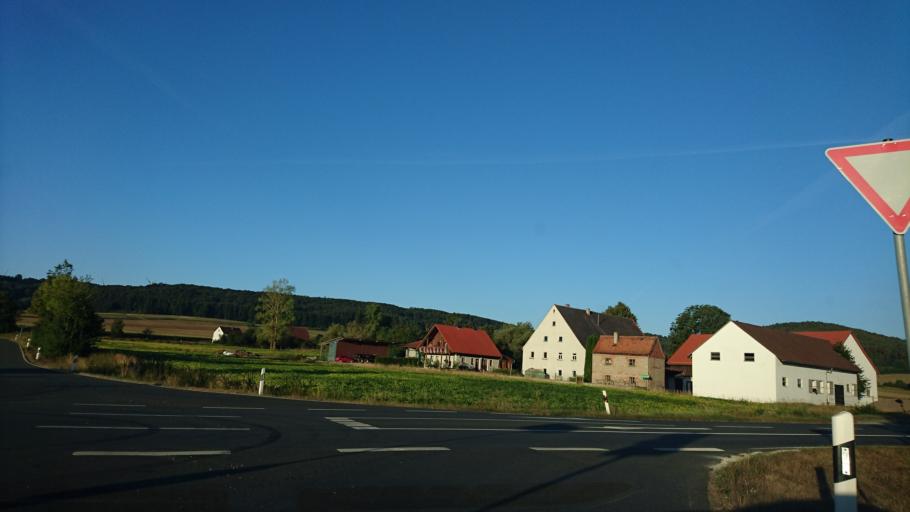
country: DE
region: Bavaria
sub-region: Regierungsbezirk Mittelfranken
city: Thalmassing
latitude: 49.0826
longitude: 11.2497
